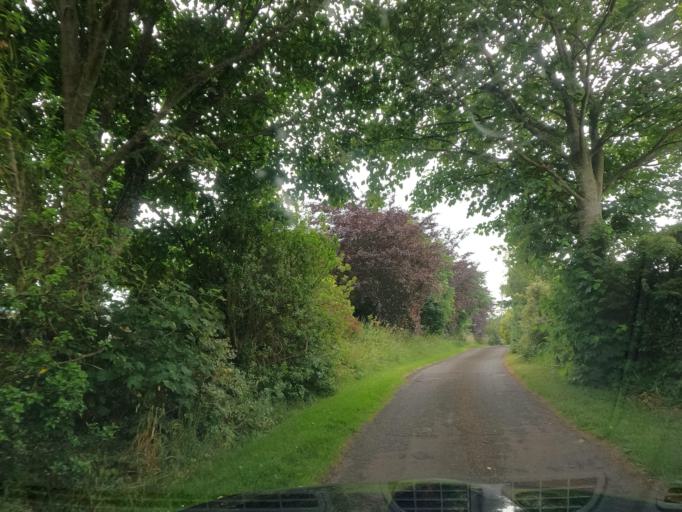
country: GB
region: England
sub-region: Northumberland
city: Lowick
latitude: 55.6518
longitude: -1.9083
